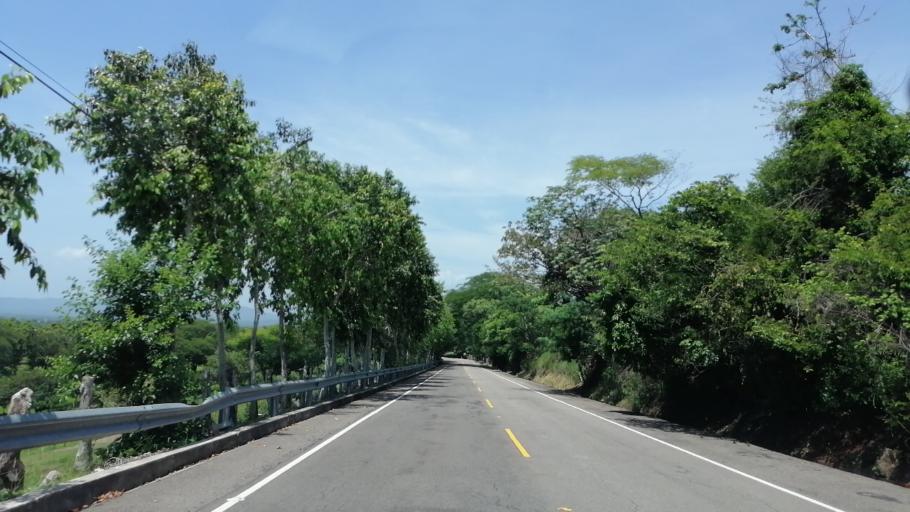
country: SV
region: Chalatenango
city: Nueva Concepcion
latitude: 14.1507
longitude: -89.3055
